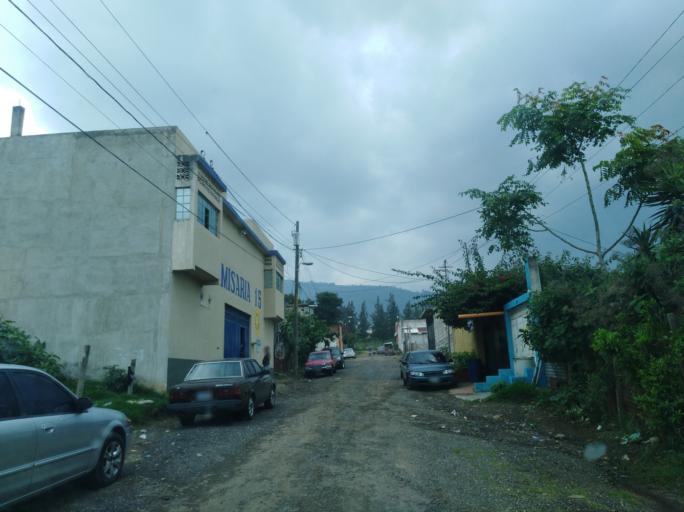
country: GT
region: Guatemala
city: Villa Nueva
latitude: 14.5265
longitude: -90.6199
